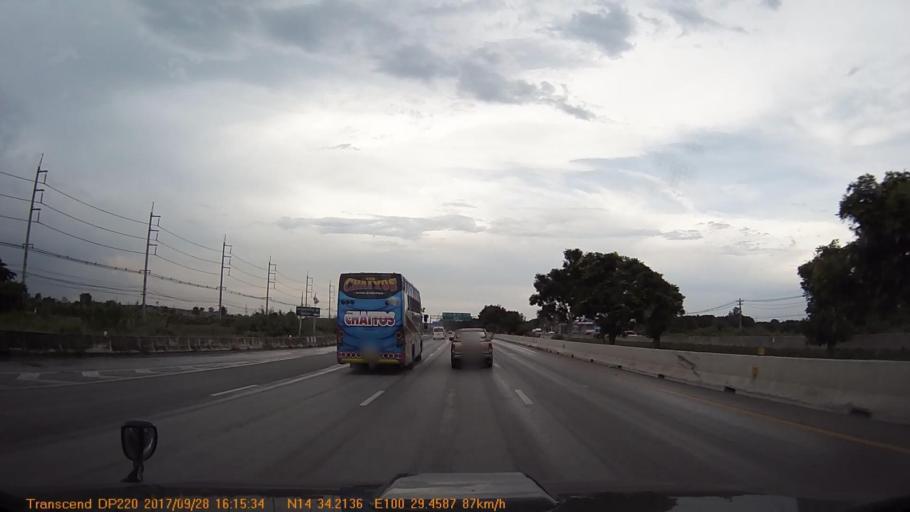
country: TH
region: Ang Thong
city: Ang Thong
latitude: 14.5706
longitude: 100.4907
